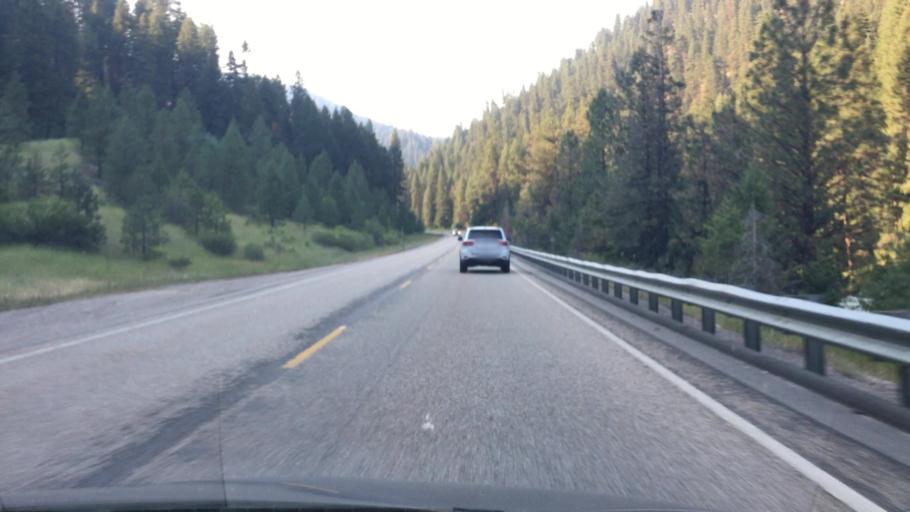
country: US
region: Idaho
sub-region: Valley County
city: Cascade
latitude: 44.1611
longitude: -116.1180
